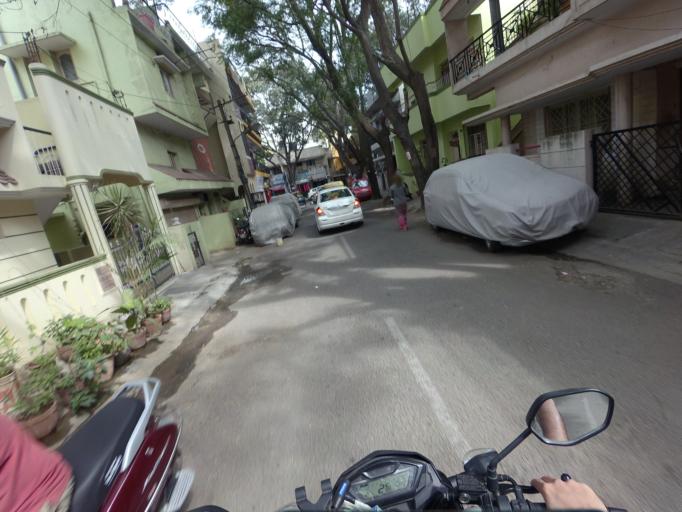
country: IN
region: Karnataka
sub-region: Bangalore Urban
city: Bangalore
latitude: 12.9688
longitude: 77.5356
